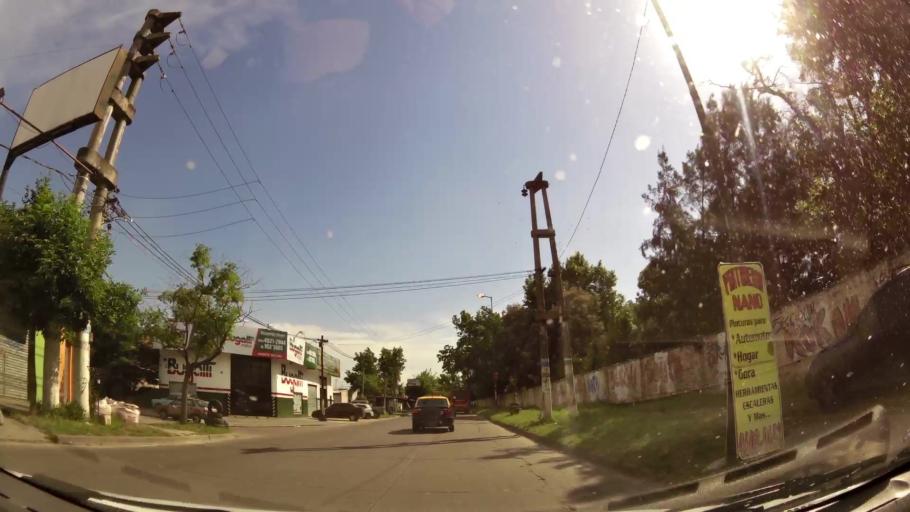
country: AR
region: Buenos Aires
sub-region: Partido de Merlo
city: Merlo
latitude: -34.6380
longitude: -58.7136
